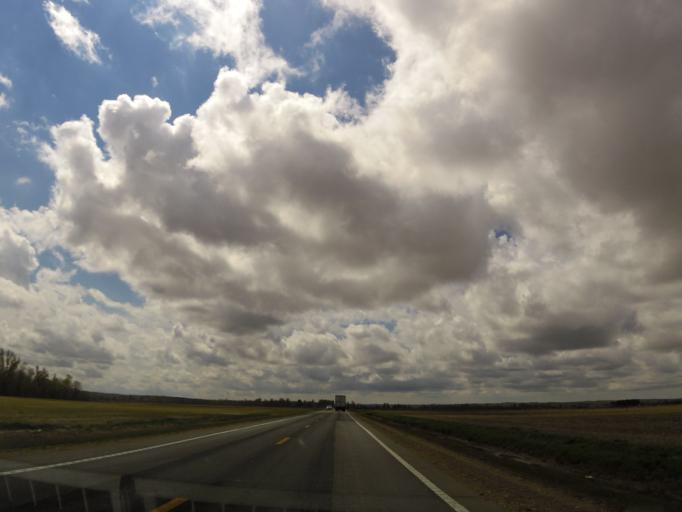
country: US
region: Arkansas
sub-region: Clay County
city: Corning
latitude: 36.2648
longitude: -90.5348
